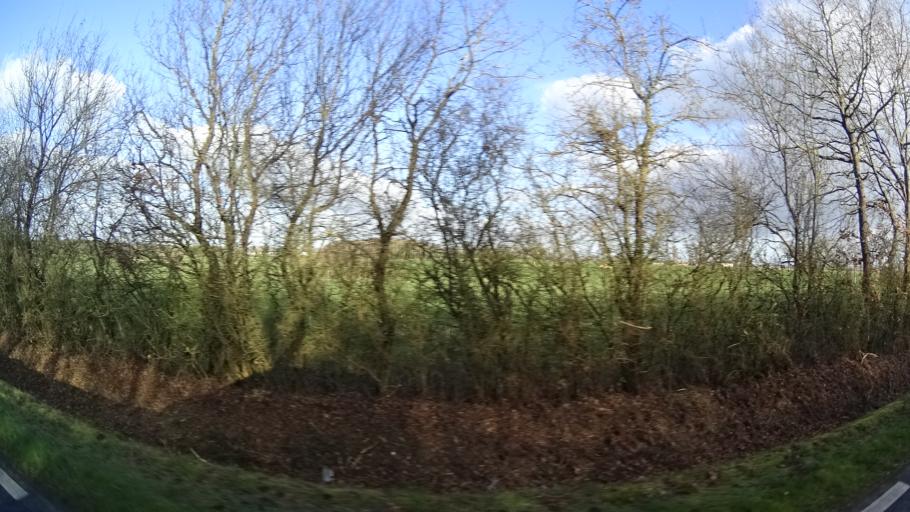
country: FR
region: Pays de la Loire
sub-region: Departement de la Loire-Atlantique
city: Plesse
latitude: 47.5203
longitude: -1.8928
